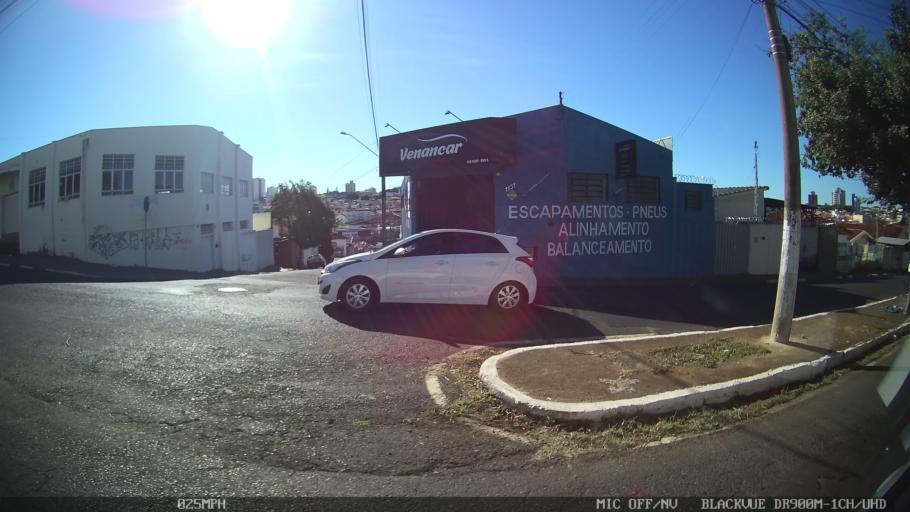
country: BR
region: Sao Paulo
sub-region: Franca
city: Franca
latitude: -20.5467
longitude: -47.4104
